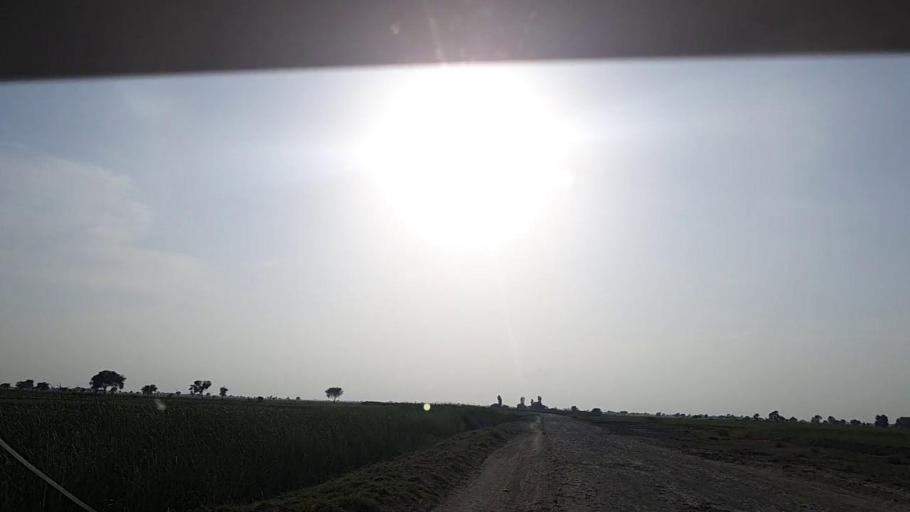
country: PK
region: Sindh
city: Khanpur
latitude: 27.8355
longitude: 69.3729
